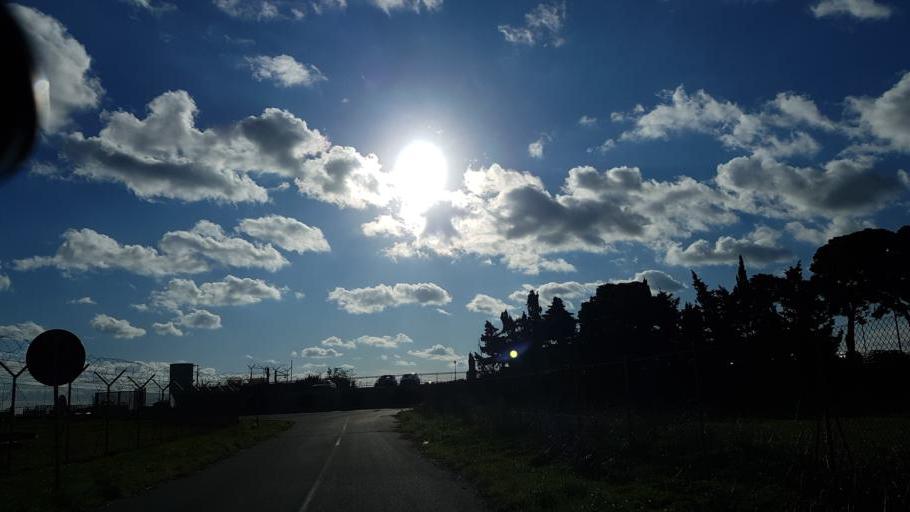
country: IT
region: Apulia
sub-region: Provincia di Brindisi
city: Materdomini
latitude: 40.6607
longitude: 17.9411
